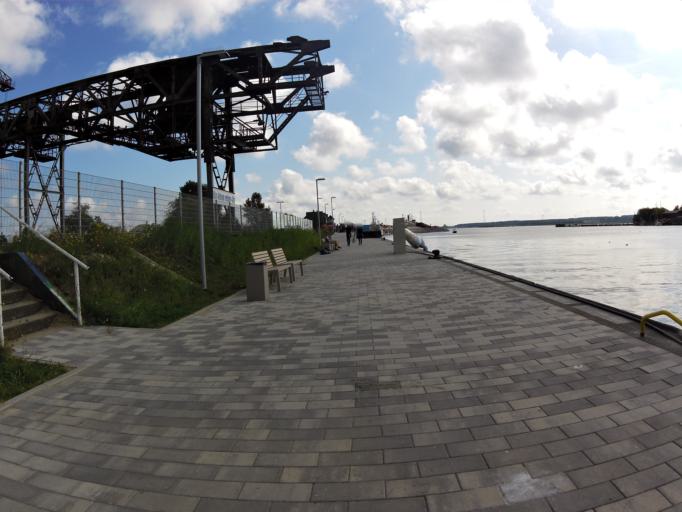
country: DE
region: Mecklenburg-Vorpommern
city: Kroslin
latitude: 54.1374
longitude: 13.7649
